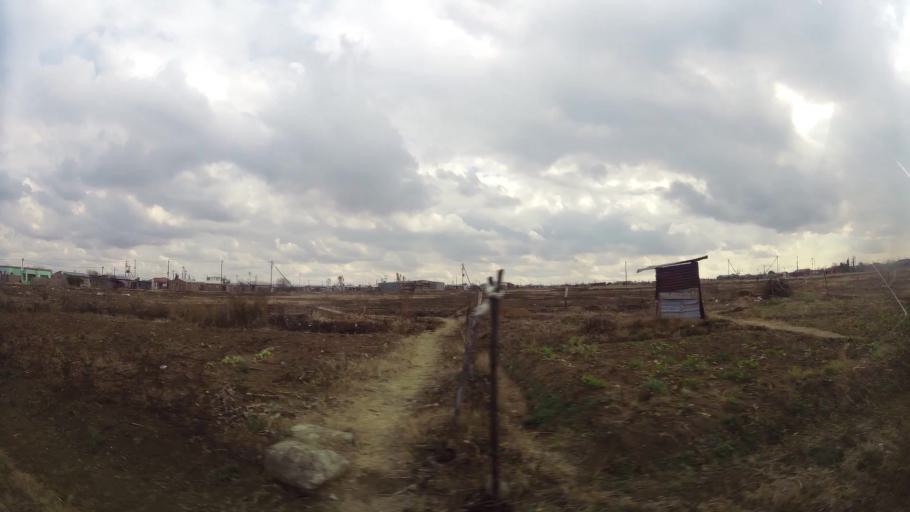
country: ZA
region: Orange Free State
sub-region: Fezile Dabi District Municipality
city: Sasolburg
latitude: -26.8636
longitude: 27.8989
